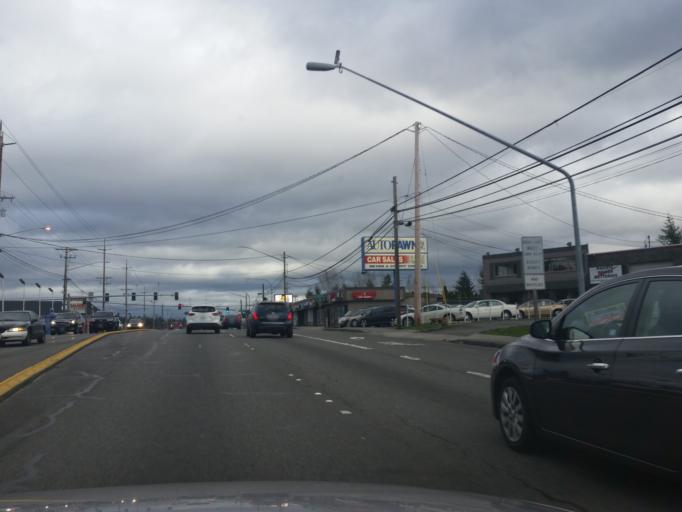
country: US
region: Washington
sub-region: Snohomish County
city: Lynnwood
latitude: 47.8165
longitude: -122.3192
